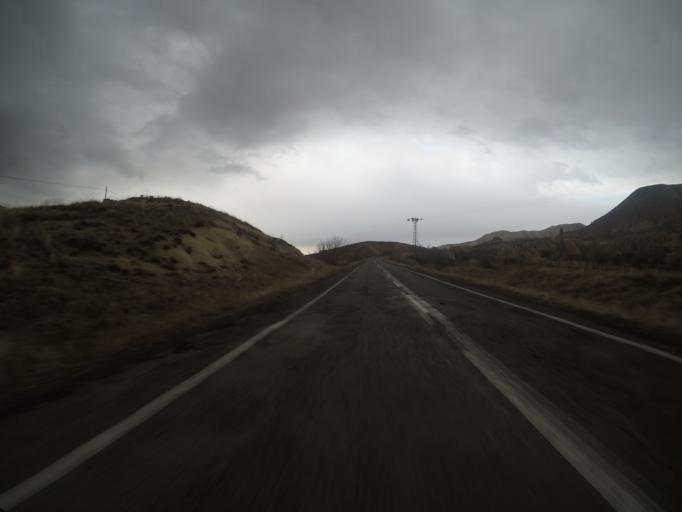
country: TR
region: Nevsehir
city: Avanos
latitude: 38.6794
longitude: 34.8489
